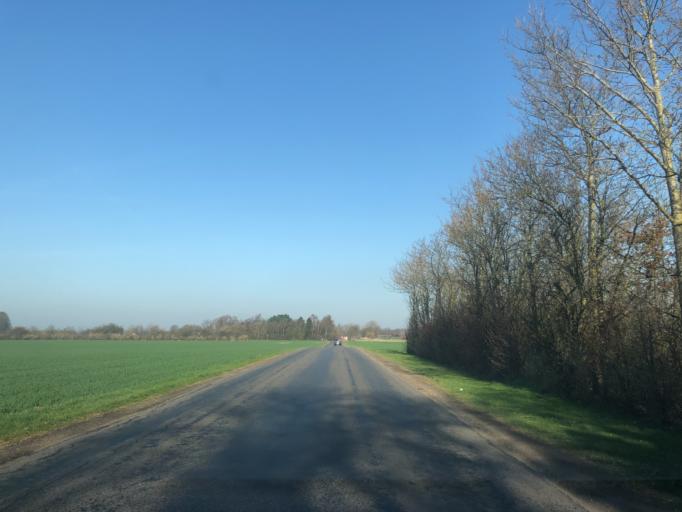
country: DK
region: Zealand
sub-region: Stevns Kommune
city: Store Heddinge
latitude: 55.2799
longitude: 12.3192
